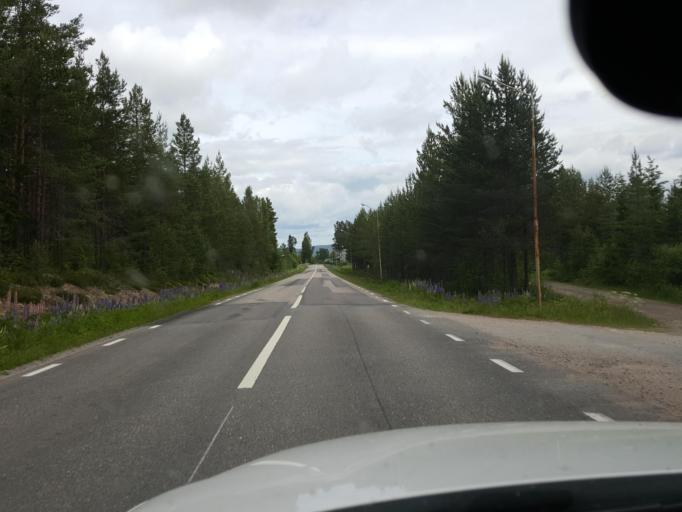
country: SE
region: Gaevleborg
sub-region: Ljusdals Kommun
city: Farila
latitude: 61.8012
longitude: 15.7158
